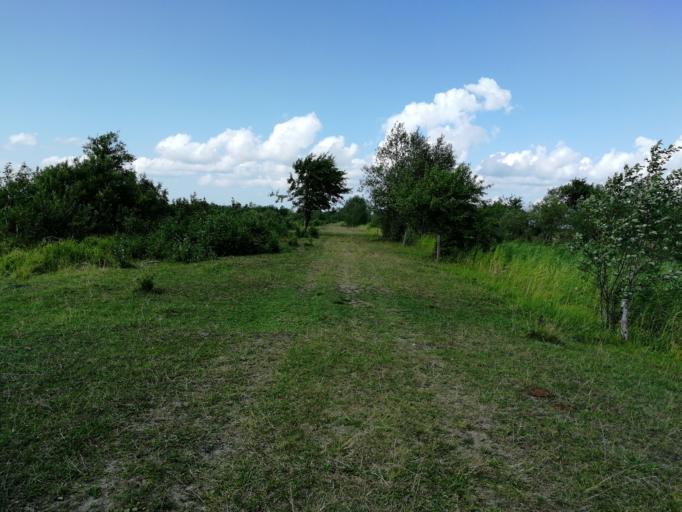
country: EE
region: Laeaene
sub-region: Lihula vald
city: Lihula
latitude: 58.7230
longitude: 23.8083
